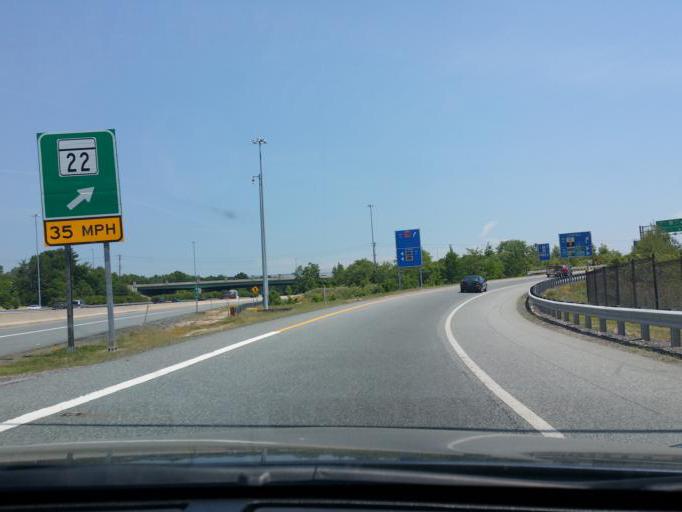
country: US
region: Maryland
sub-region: Harford County
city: Aberdeen
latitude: 39.5241
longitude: -76.1946
